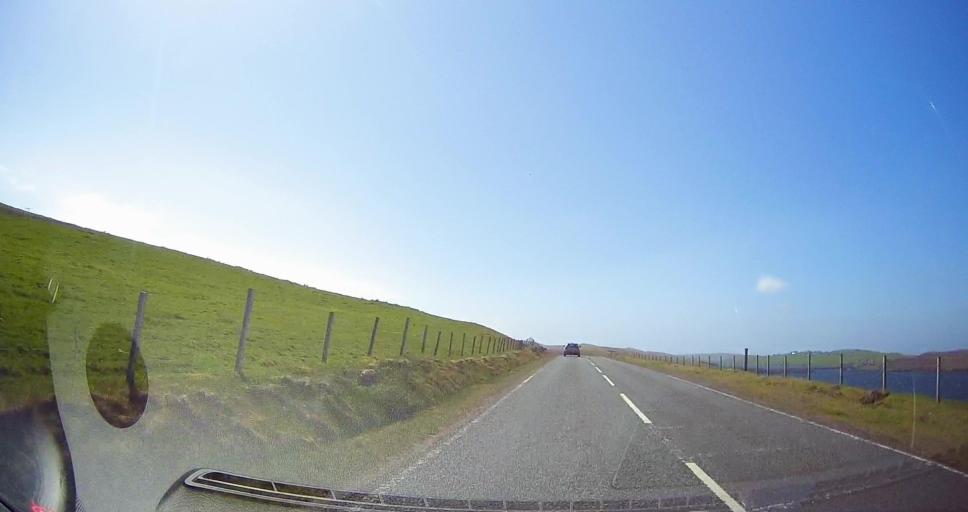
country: GB
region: Scotland
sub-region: Shetland Islands
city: Sandwick
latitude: 60.1137
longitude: -1.2945
